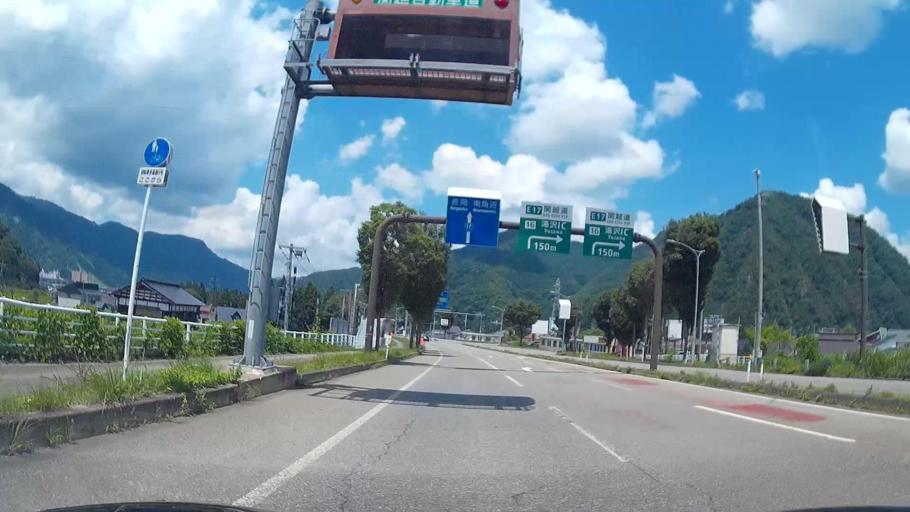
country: JP
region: Niigata
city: Shiozawa
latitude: 36.9291
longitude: 138.8237
